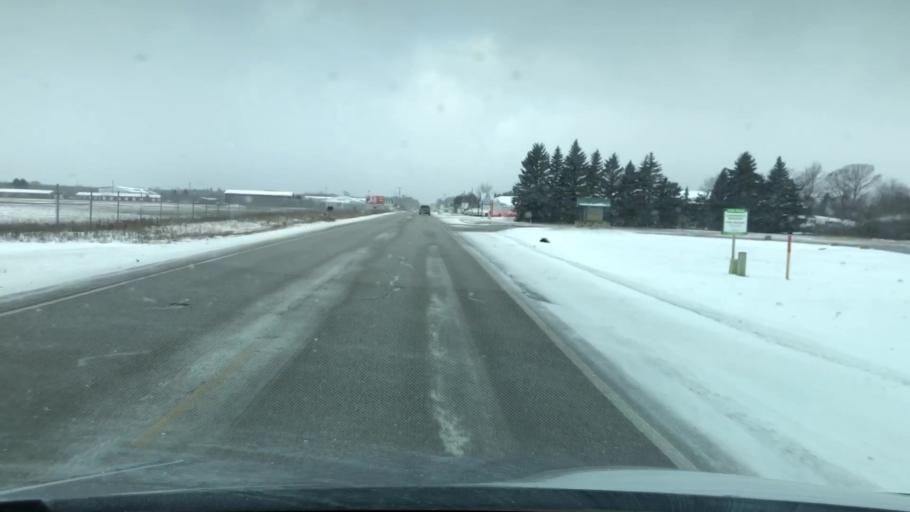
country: US
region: Michigan
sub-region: Wexford County
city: Cadillac
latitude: 44.2813
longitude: -85.4216
